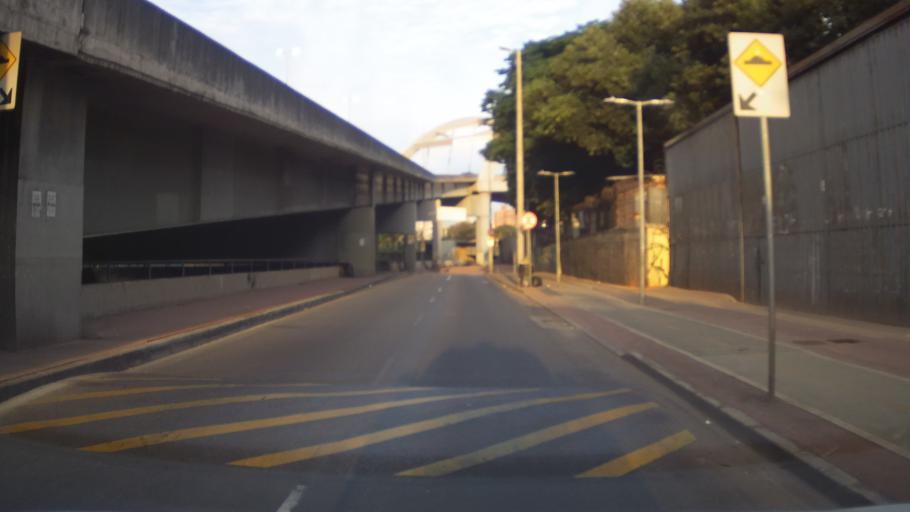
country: BR
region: Minas Gerais
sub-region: Belo Horizonte
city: Belo Horizonte
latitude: -19.9188
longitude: -43.9590
